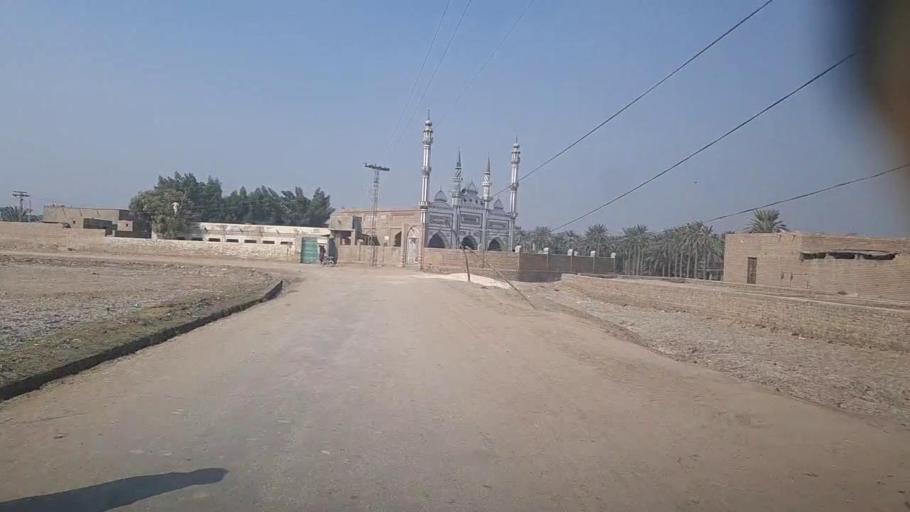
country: PK
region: Sindh
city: Khairpur
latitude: 27.5524
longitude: 68.7823
